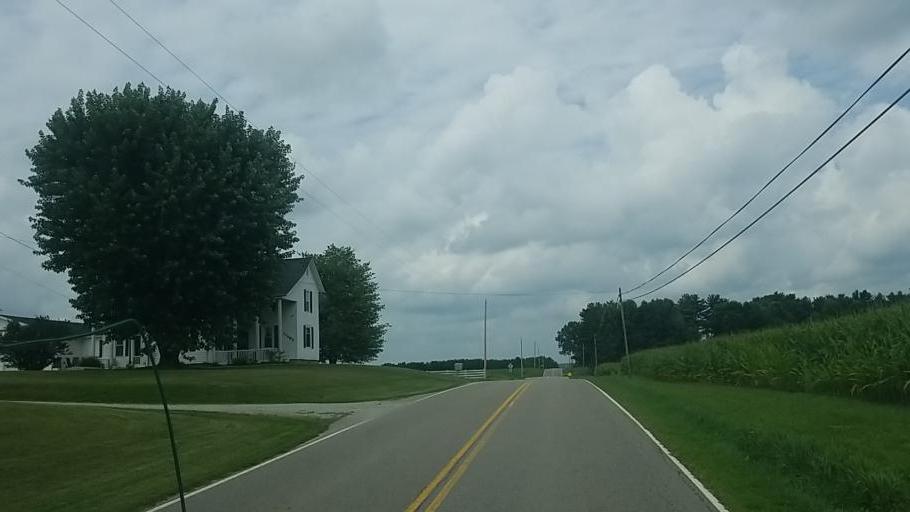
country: US
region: Ohio
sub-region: Licking County
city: Utica
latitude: 40.2140
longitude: -82.3666
